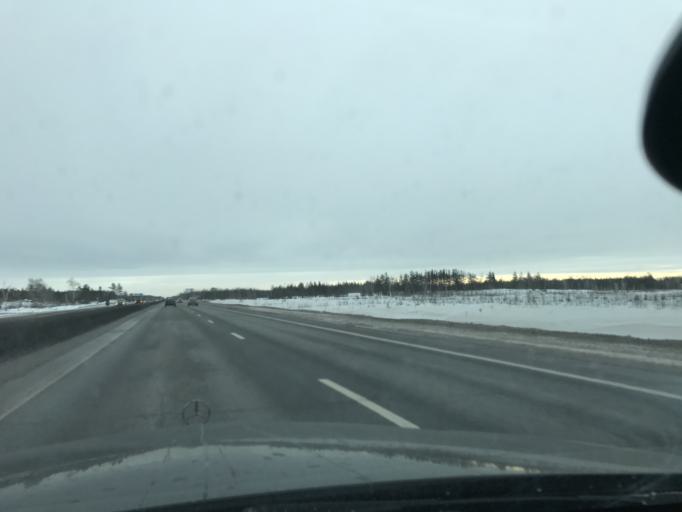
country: RU
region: Nizjnij Novgorod
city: Dzerzhinsk
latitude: 56.2998
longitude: 43.5123
